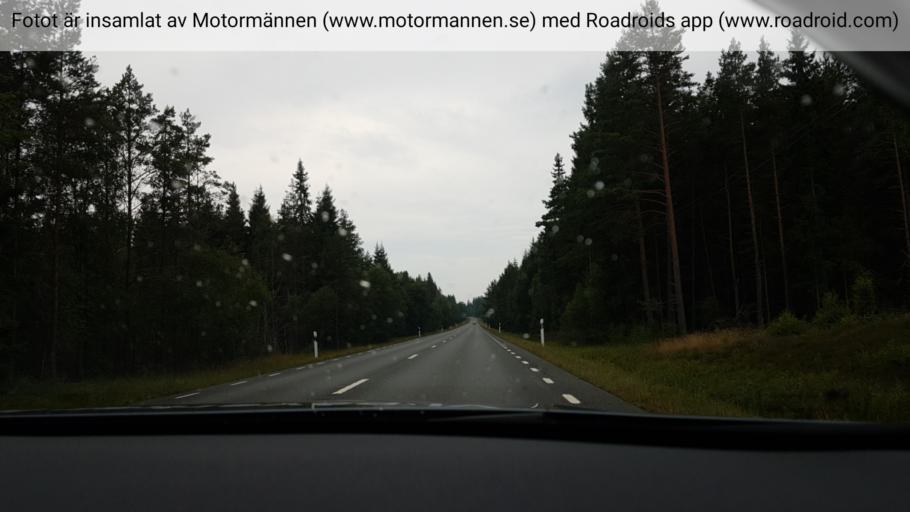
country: SE
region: Joenkoeping
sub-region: Savsjo Kommun
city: Vrigstad
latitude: 57.3623
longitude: 14.4131
